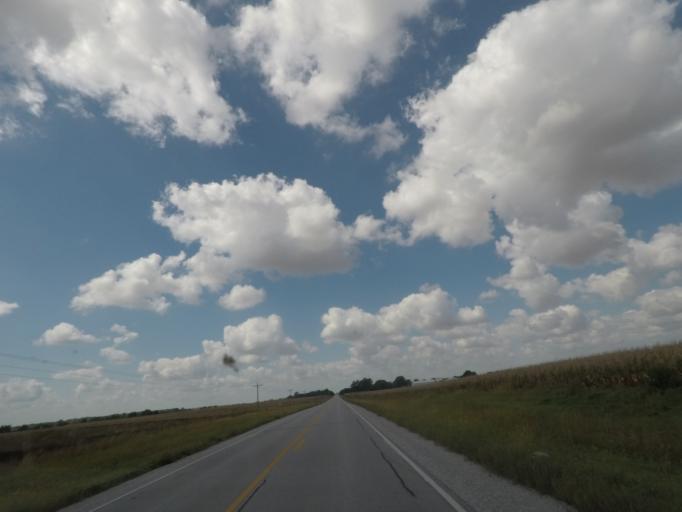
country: US
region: Iowa
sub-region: Story County
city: Nevada
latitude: 42.0226
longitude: -93.3608
